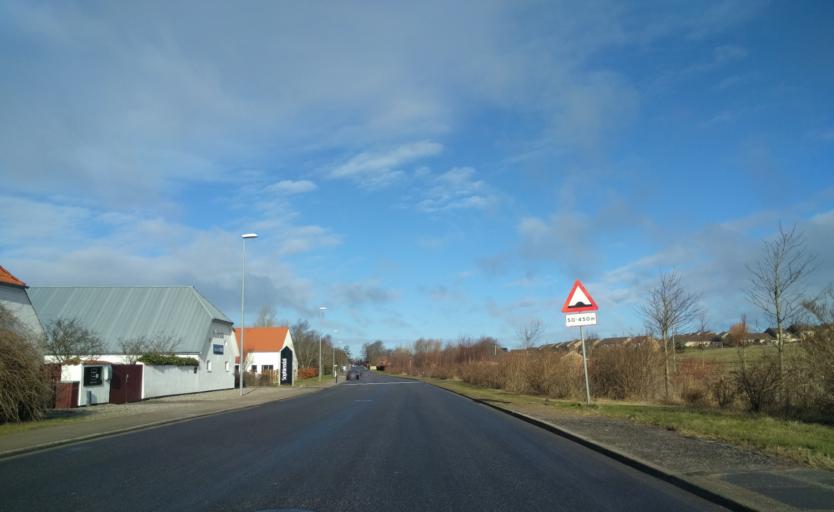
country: DK
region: North Denmark
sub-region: Alborg Kommune
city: Aalborg
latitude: 57.0182
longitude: 9.8751
